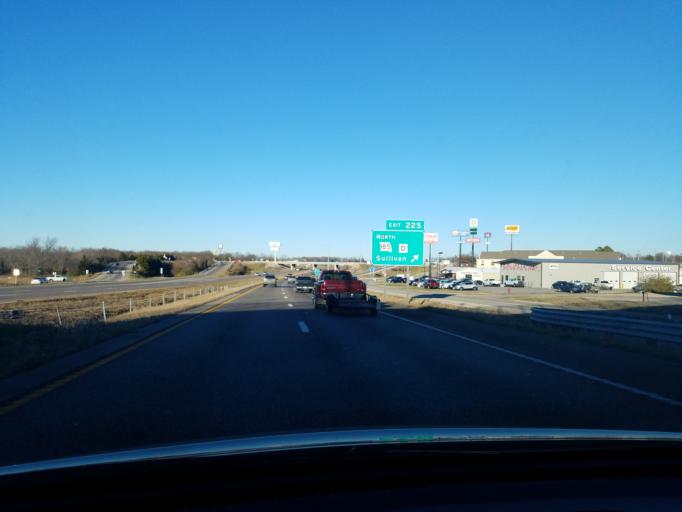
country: US
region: Missouri
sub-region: Franklin County
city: Sullivan
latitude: 38.2085
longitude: -91.1747
